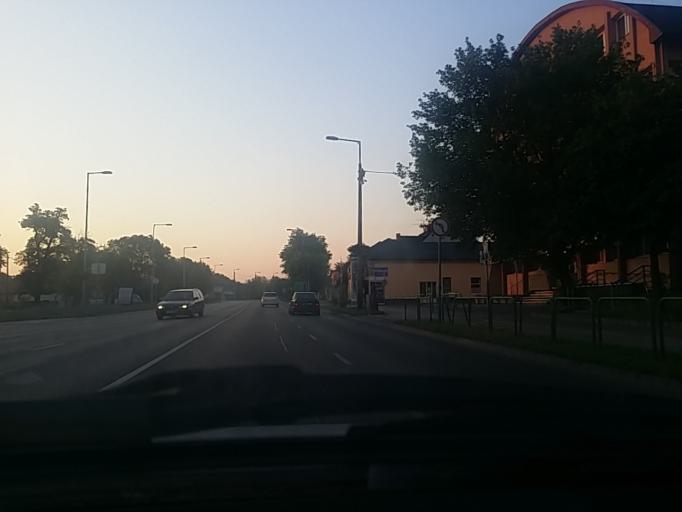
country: HU
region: Budapest
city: Budapest XVII. keruelet
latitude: 47.4793
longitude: 19.2572
